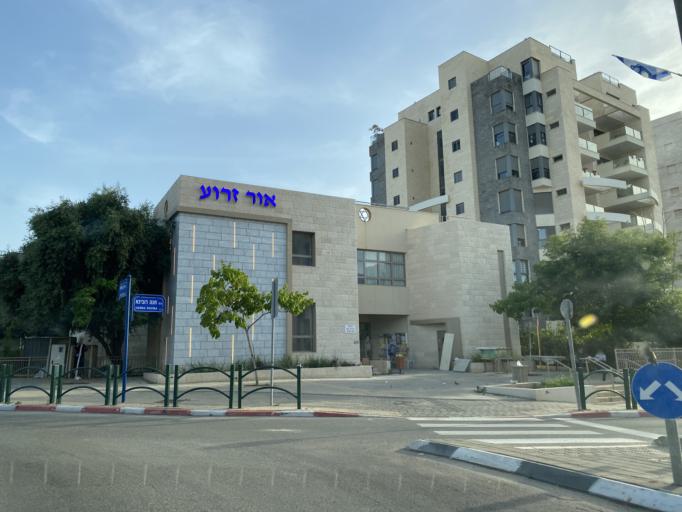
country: IL
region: Tel Aviv
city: Herzliyya
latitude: 32.1670
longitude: 34.8309
